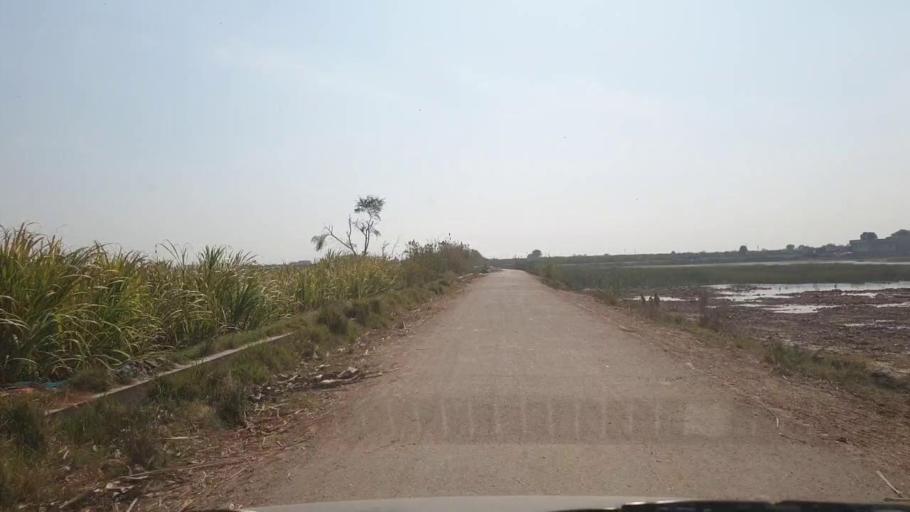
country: PK
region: Sindh
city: Chambar
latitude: 25.3587
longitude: 68.8218
